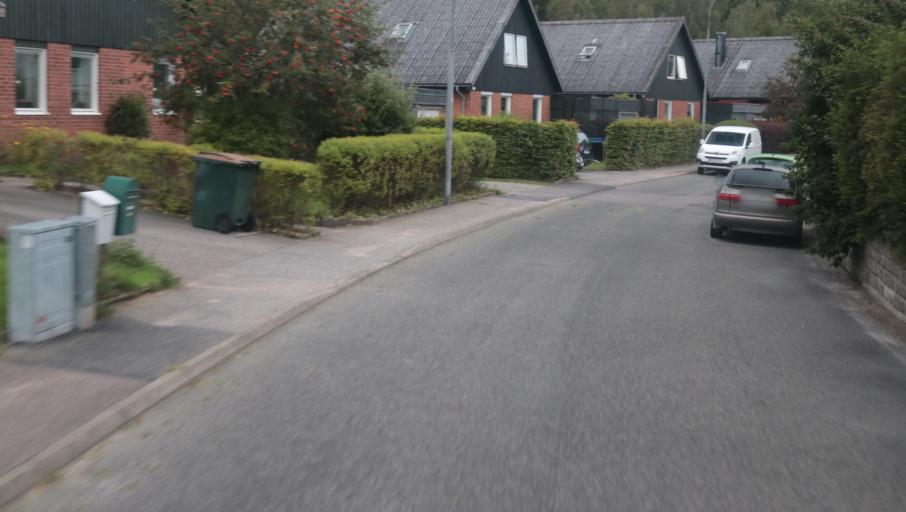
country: SE
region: Blekinge
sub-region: Karlshamns Kommun
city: Karlshamn
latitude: 56.1703
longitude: 14.8827
